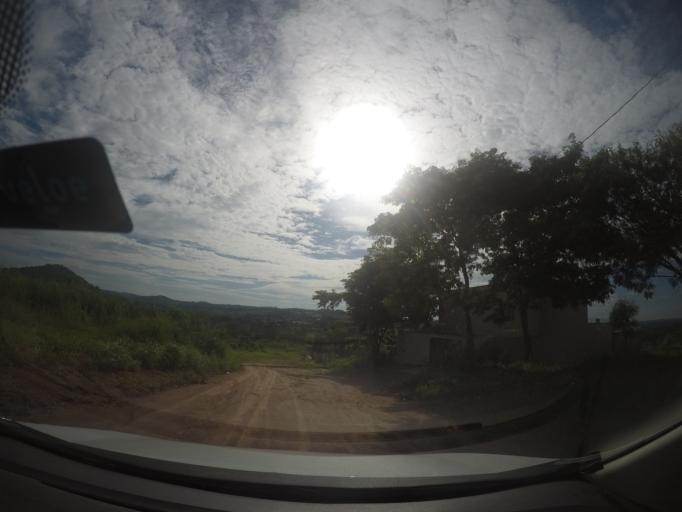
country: BR
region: Goias
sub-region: Goiania
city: Goiania
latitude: -16.6939
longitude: -49.1980
